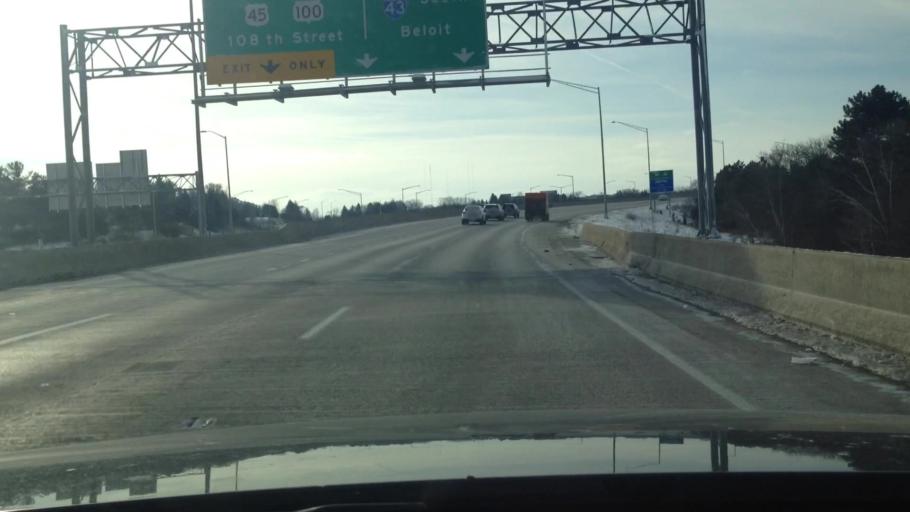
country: US
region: Wisconsin
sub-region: Milwaukee County
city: Hales Corners
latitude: 42.9586
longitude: -88.0427
